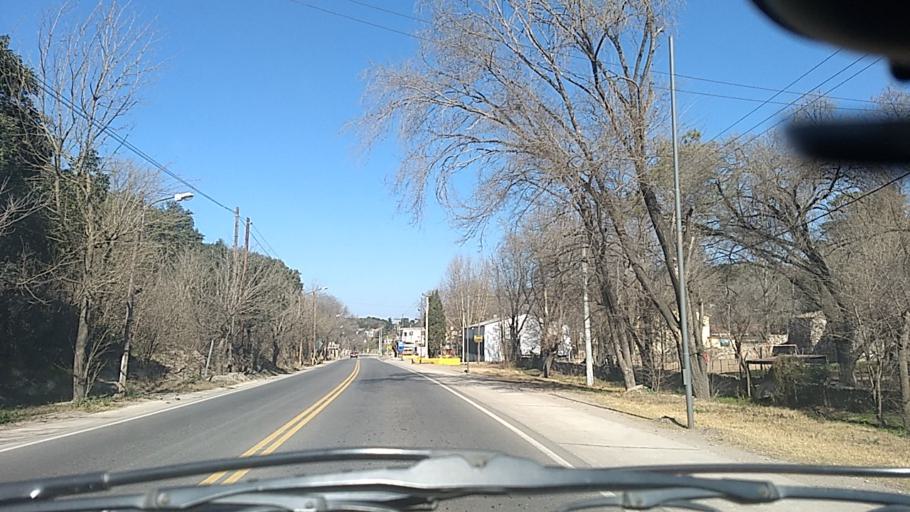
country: AR
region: Cordoba
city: Salsipuedes
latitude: -31.1029
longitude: -64.2920
